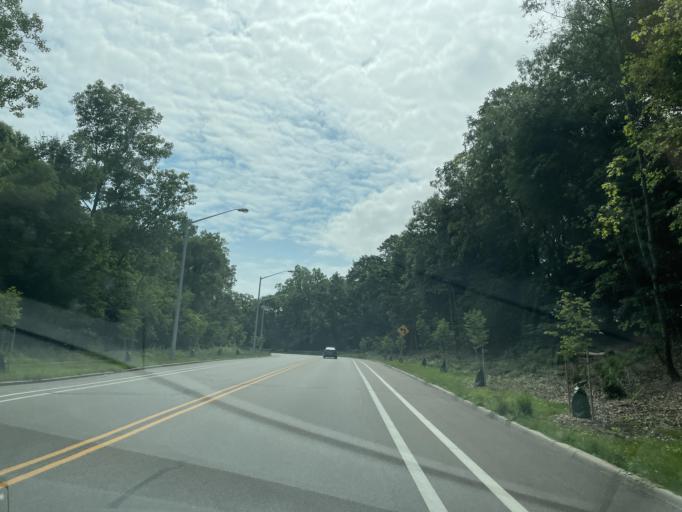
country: US
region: Michigan
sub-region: Kent County
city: East Grand Rapids
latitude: 42.9188
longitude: -85.6260
